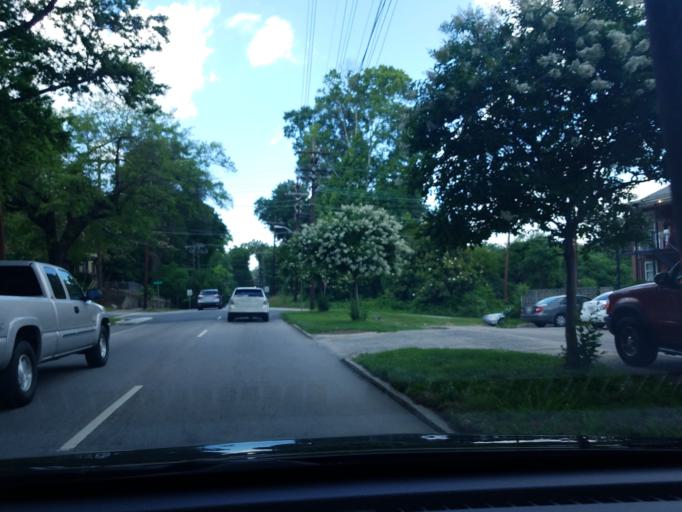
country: US
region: North Carolina
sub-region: Durham County
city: Durham
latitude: 36.0072
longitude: -78.9056
